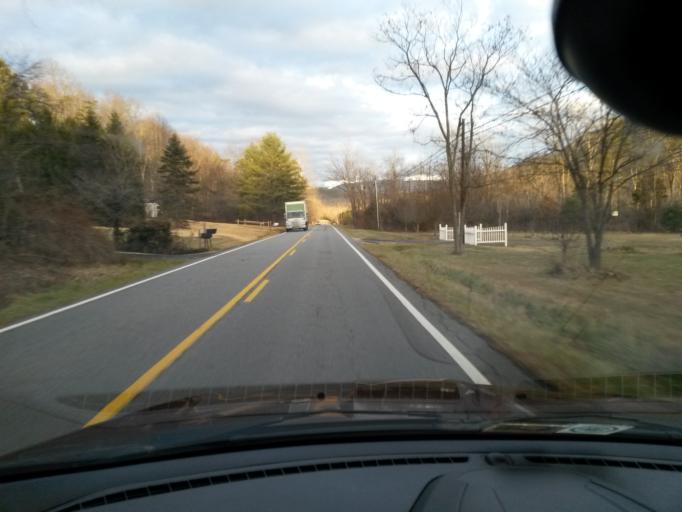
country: US
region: Virginia
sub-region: City of Covington
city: Covington
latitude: 37.7943
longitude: -80.0854
